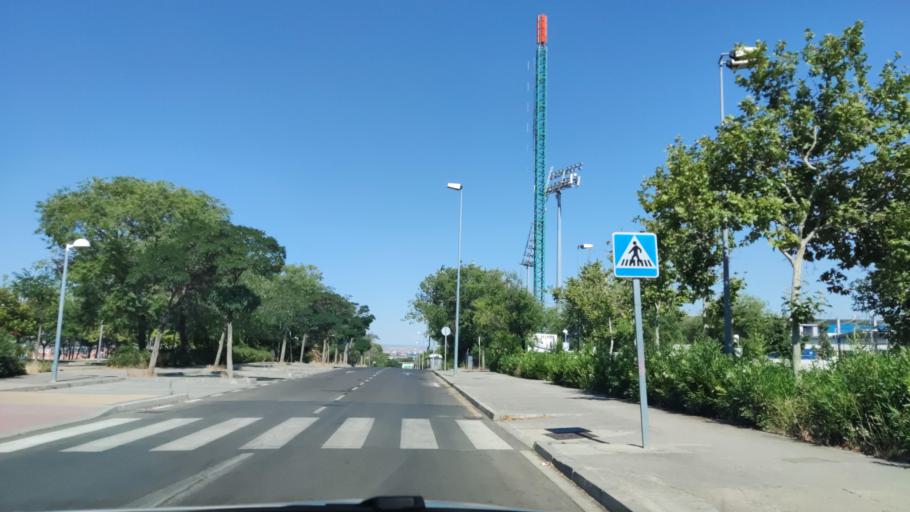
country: ES
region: Madrid
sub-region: Provincia de Madrid
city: Leganes
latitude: 40.3414
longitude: -3.7624
